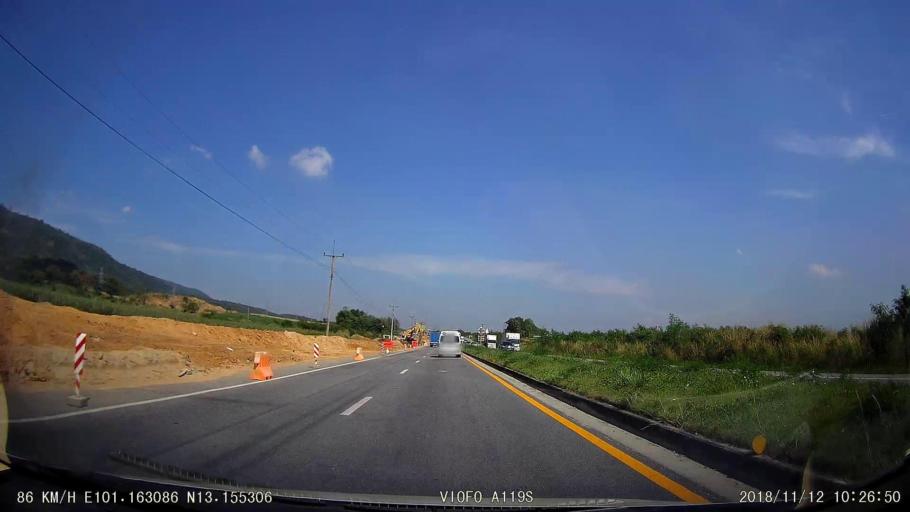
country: TH
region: Chon Buri
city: Ban Bueng
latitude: 13.1628
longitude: 101.1626
